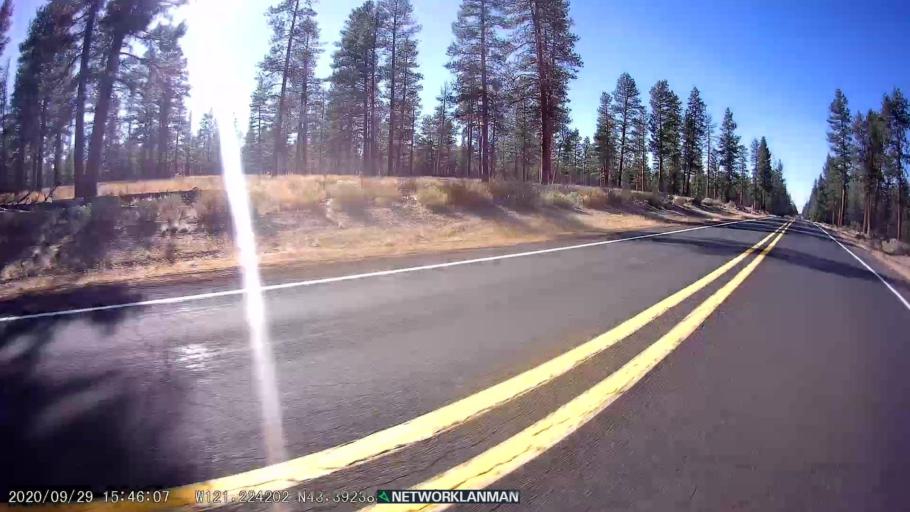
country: US
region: Oregon
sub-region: Deschutes County
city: La Pine
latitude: 43.3926
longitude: -121.2244
